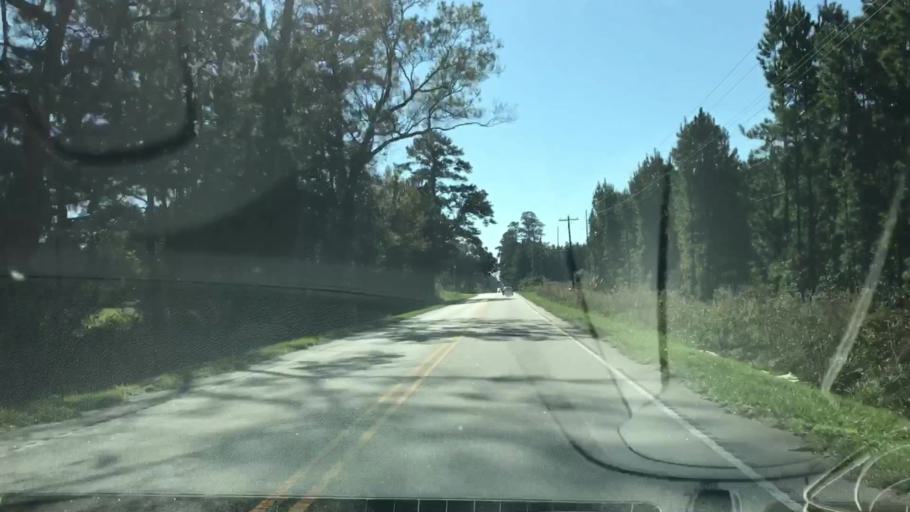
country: US
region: South Carolina
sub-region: Jasper County
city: Ridgeland
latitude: 32.5198
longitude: -80.8906
